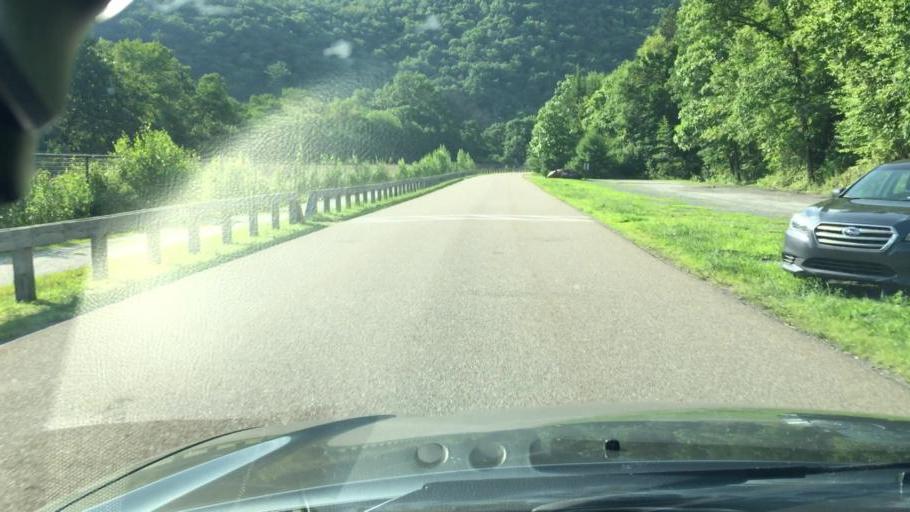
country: US
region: Pennsylvania
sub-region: Carbon County
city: Jim Thorpe
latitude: 40.8783
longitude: -75.7615
